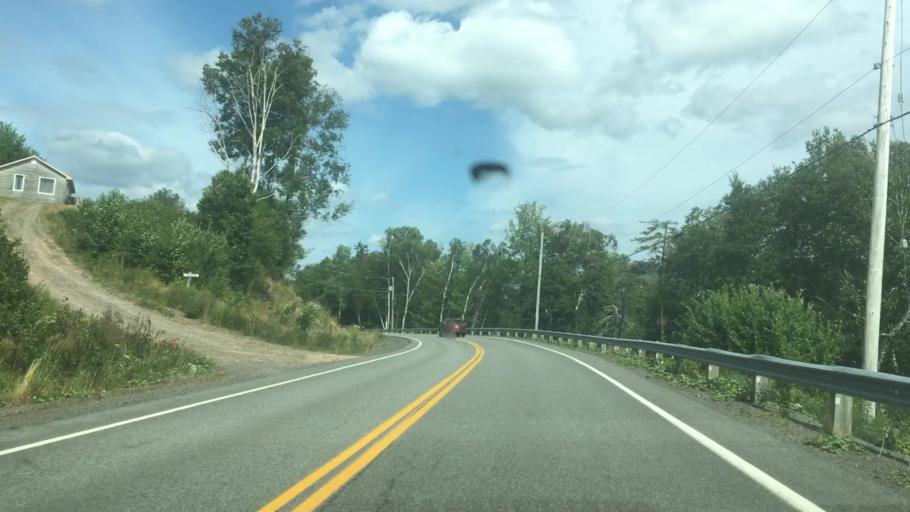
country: CA
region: Nova Scotia
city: Sydney Mines
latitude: 46.2674
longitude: -60.6086
